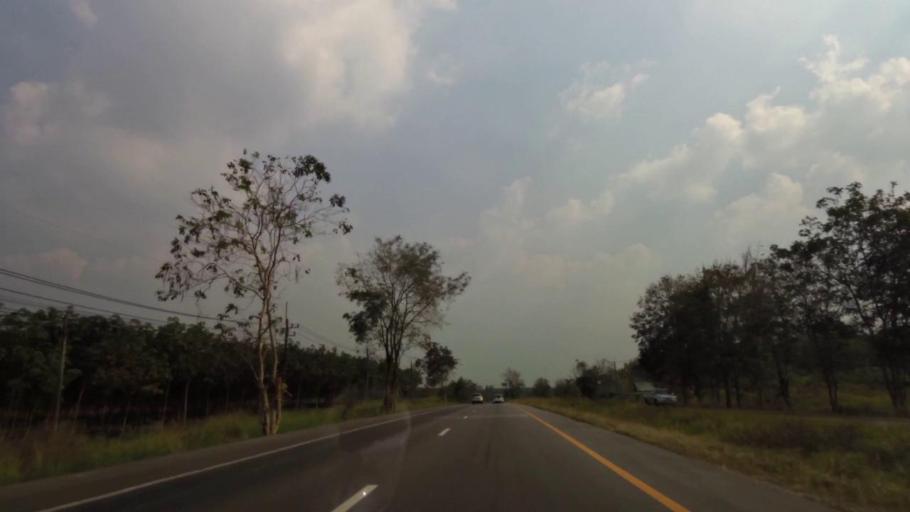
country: TH
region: Chon Buri
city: Nong Yai
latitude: 13.1203
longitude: 101.3673
